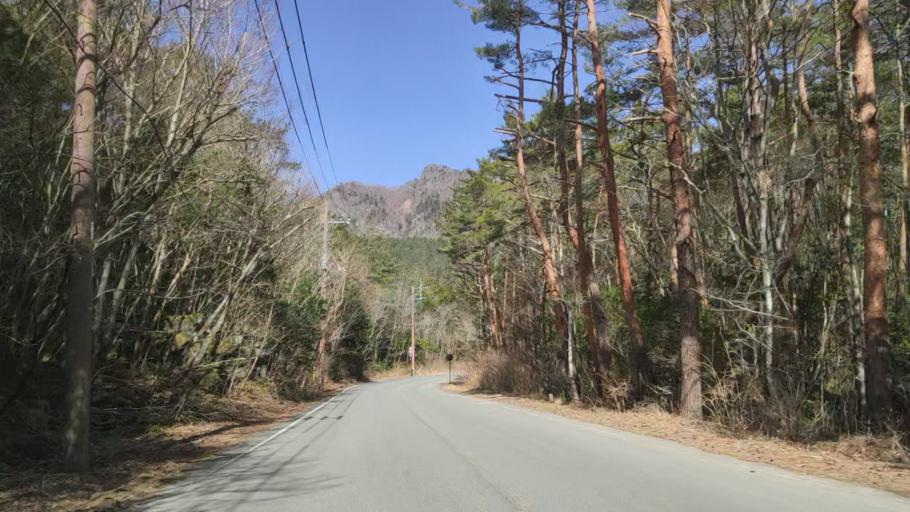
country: JP
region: Yamanashi
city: Fujikawaguchiko
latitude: 35.4981
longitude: 138.6634
